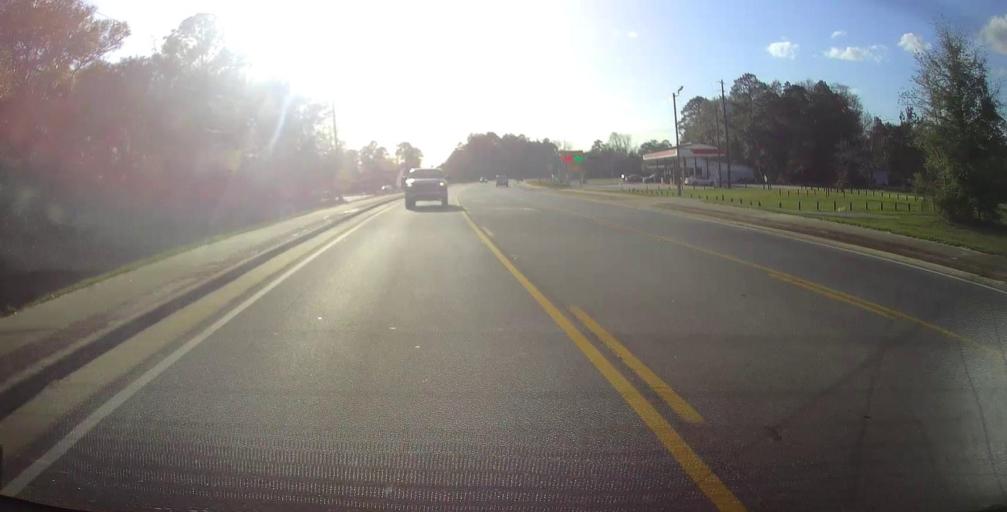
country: US
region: Georgia
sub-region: Tattnall County
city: Reidsville
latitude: 32.0807
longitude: -82.1272
